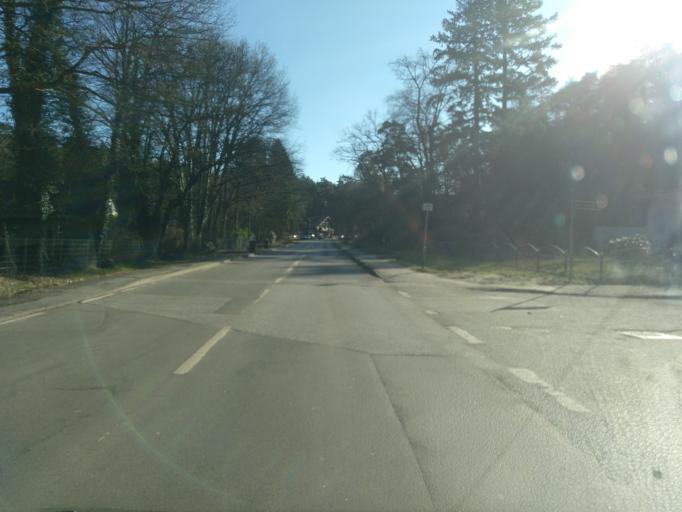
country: DE
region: Lower Saxony
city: Neu Wulmstorf
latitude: 53.4630
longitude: 9.8918
